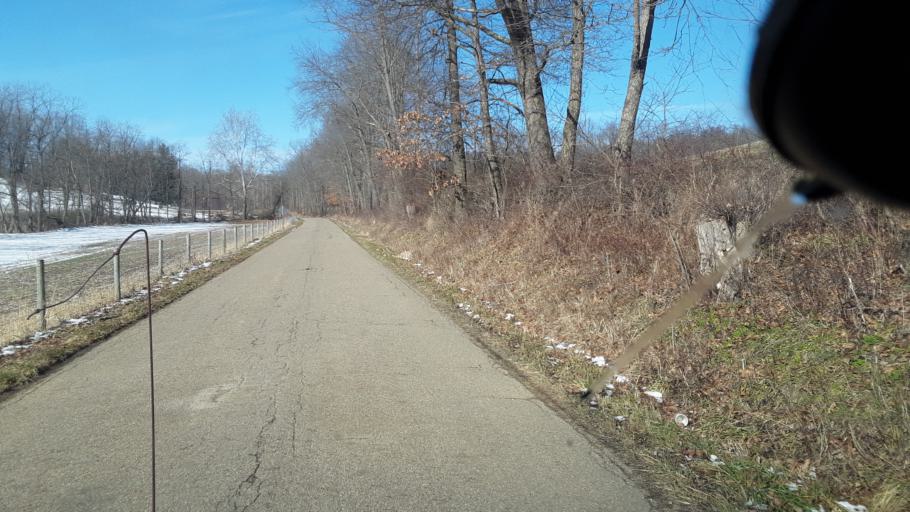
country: US
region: Ohio
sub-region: Sandusky County
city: Bellville
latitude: 40.6097
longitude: -82.4162
